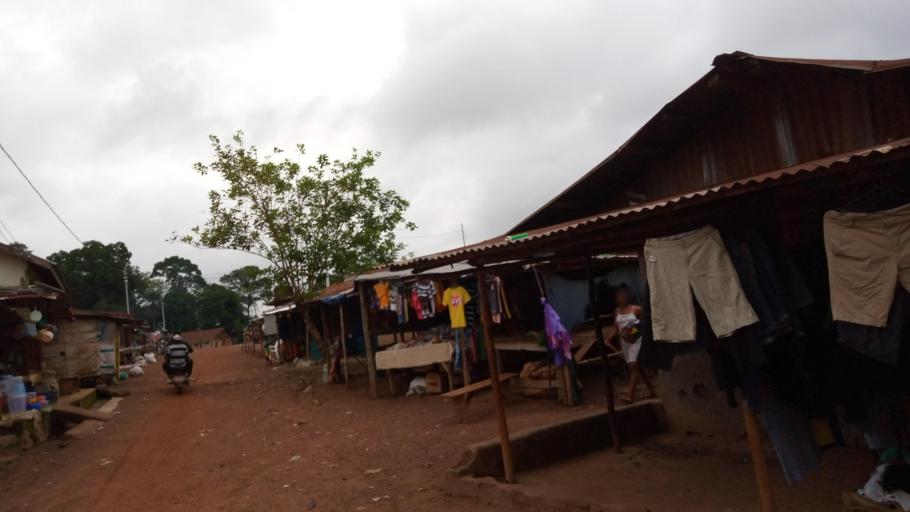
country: SL
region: Southern Province
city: Tongole
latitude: 7.4329
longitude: -11.8415
